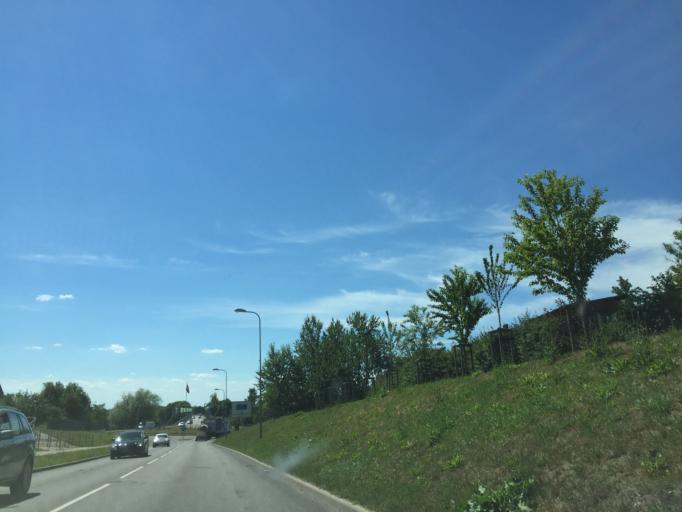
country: LV
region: Jekabpils Rajons
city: Jekabpils
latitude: 56.5032
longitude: 25.8785
